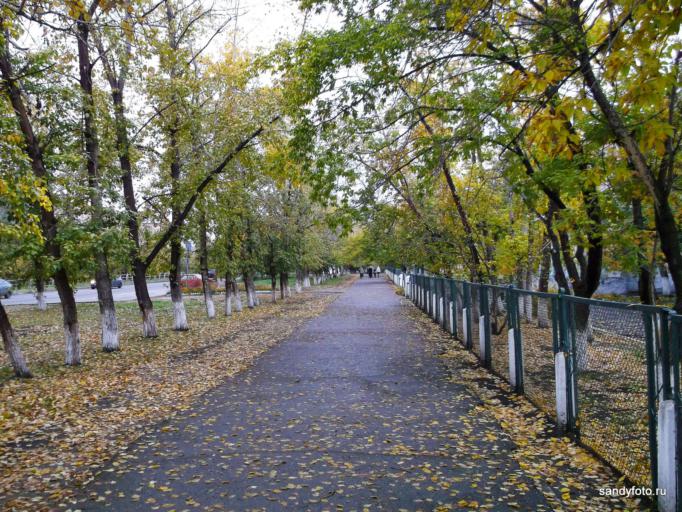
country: RU
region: Chelyabinsk
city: Troitsk
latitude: 54.0793
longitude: 61.5366
